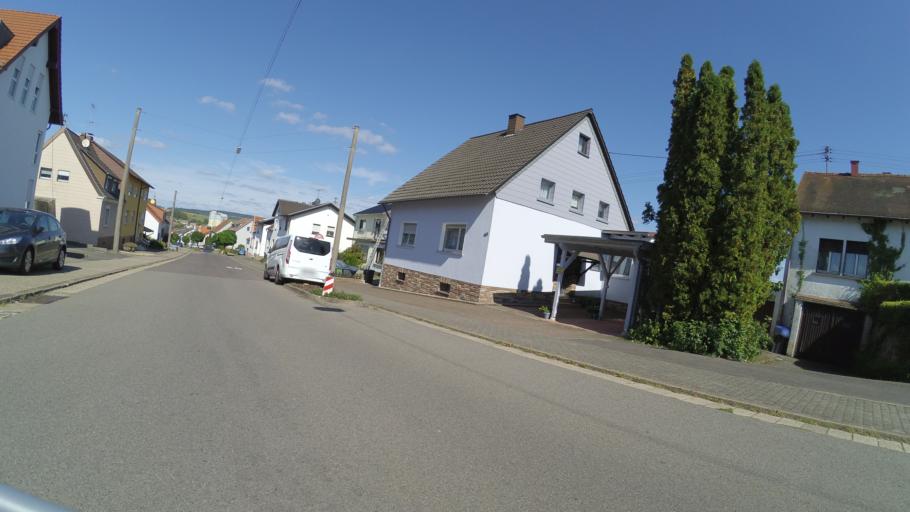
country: DE
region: Saarland
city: Lebach
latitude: 49.4024
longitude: 6.9124
